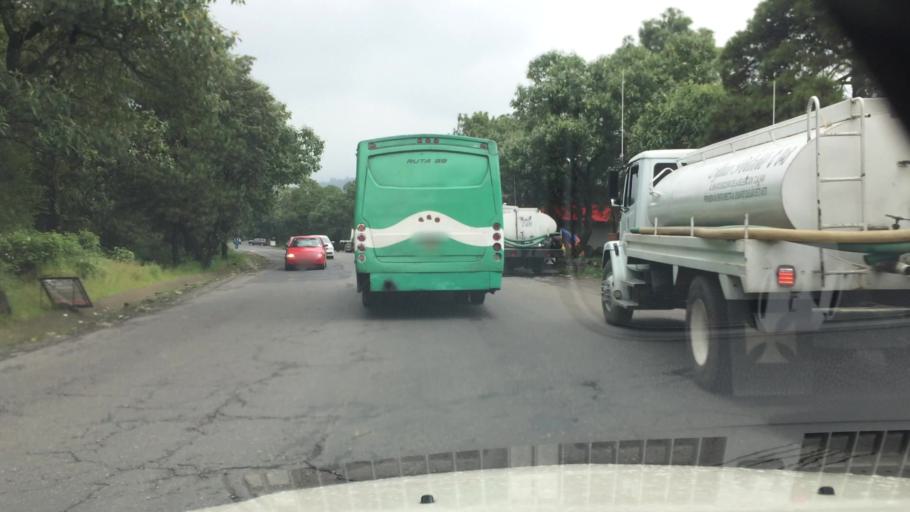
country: MX
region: Mexico City
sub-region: Tlalpan
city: Lomas de Tepemecatl
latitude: 19.2672
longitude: -99.2346
